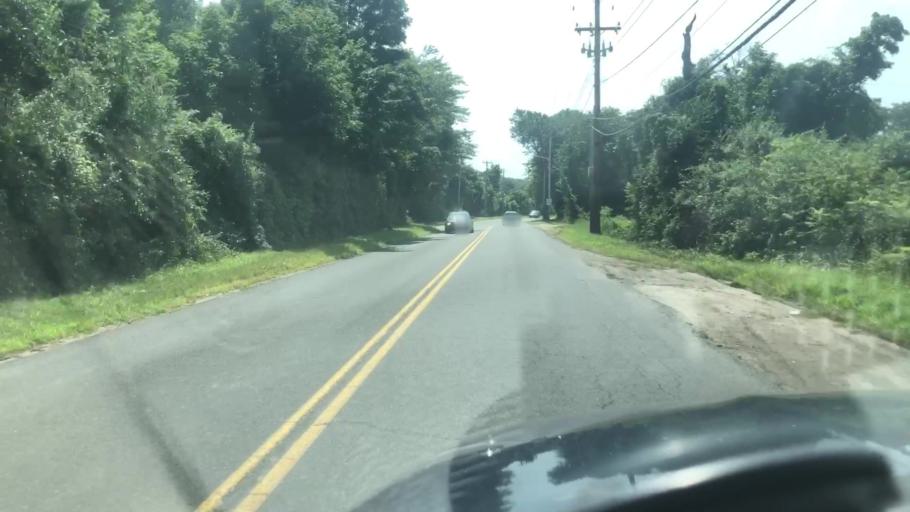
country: US
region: Massachusetts
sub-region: Hampshire County
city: Southampton
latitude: 42.1769
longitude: -72.6879
